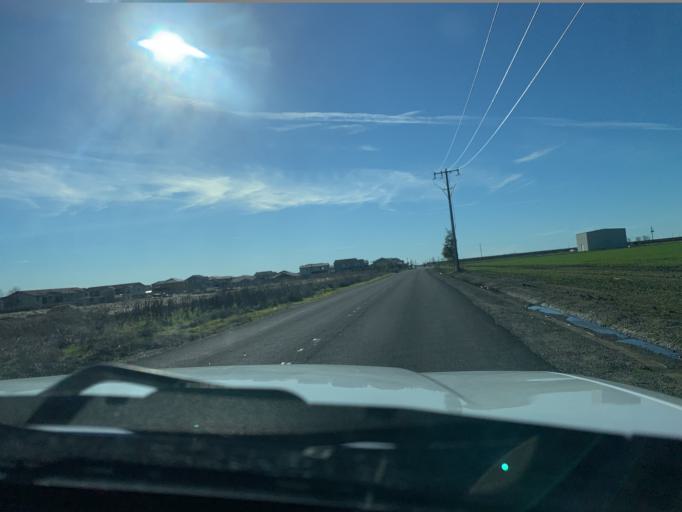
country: US
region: California
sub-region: Yolo County
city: Woodland
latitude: 38.6505
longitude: -121.7473
